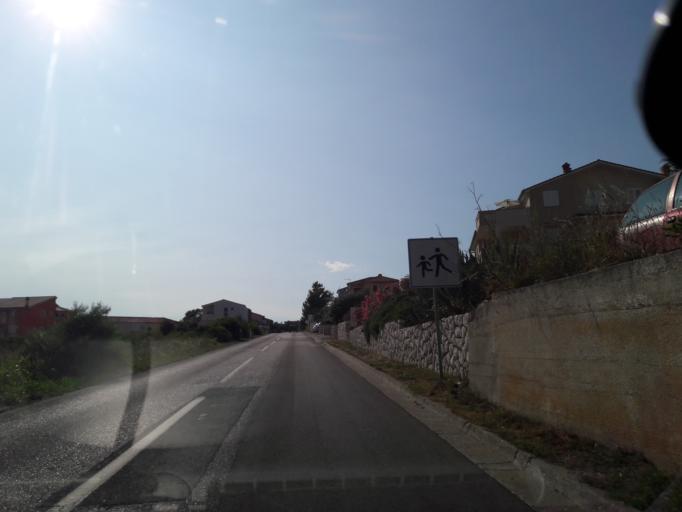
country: HR
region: Primorsko-Goranska
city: Banjol
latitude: 44.7348
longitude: 14.8069
